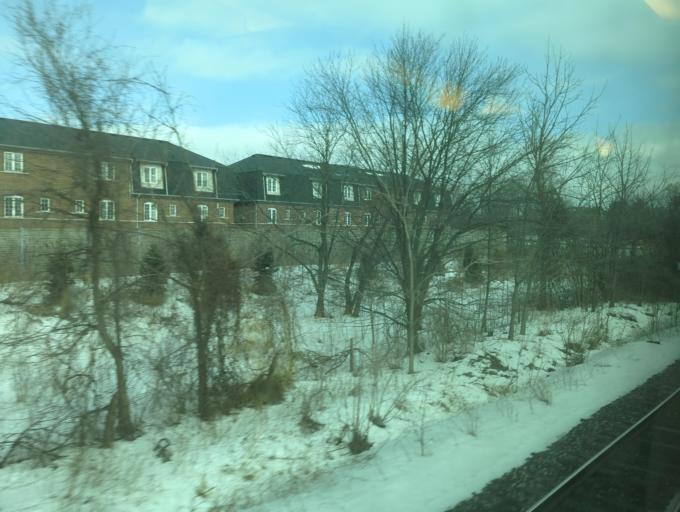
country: CA
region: Ontario
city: Etobicoke
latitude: 43.5825
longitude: -79.5582
